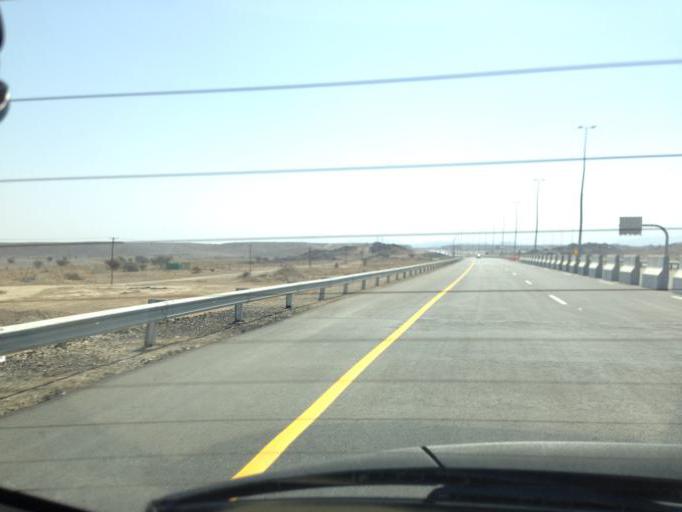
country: OM
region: Al Batinah
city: Rustaq
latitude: 23.5561
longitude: 57.5020
